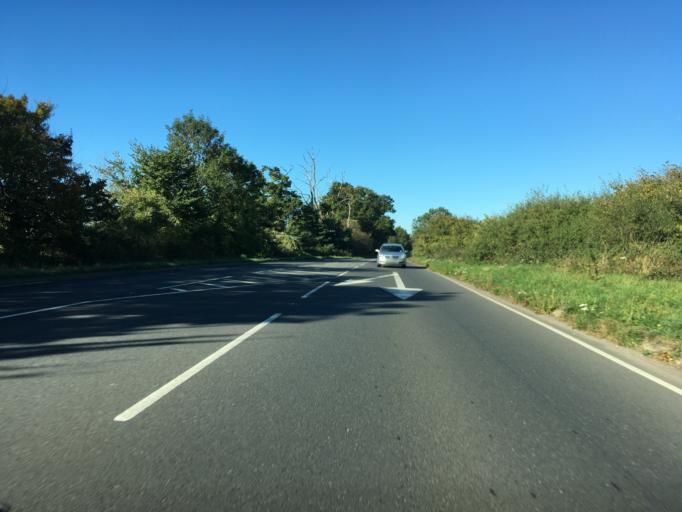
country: GB
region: England
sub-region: Wiltshire
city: Biddestone
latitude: 51.4713
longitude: -2.1971
